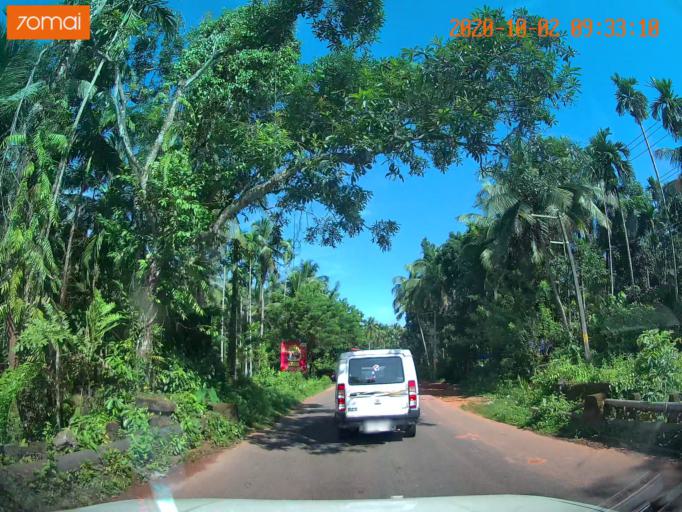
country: IN
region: Kerala
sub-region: Kozhikode
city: Nadapuram
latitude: 11.6292
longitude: 75.7524
